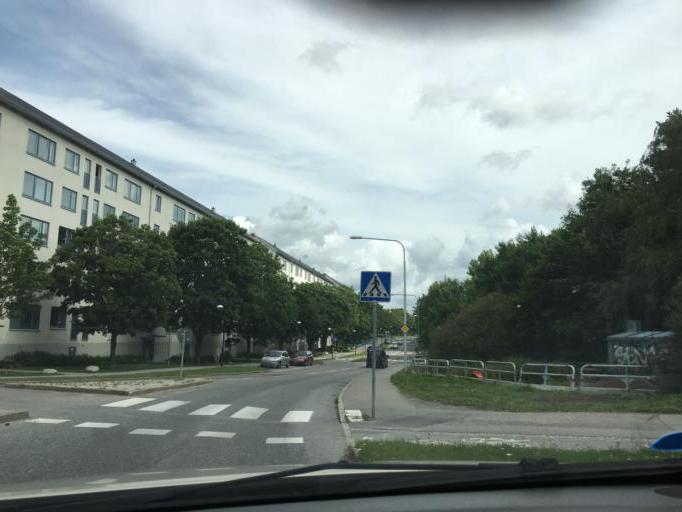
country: SE
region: Stockholm
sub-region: Stockholms Kommun
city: Bromma
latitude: 59.3556
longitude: 17.8878
